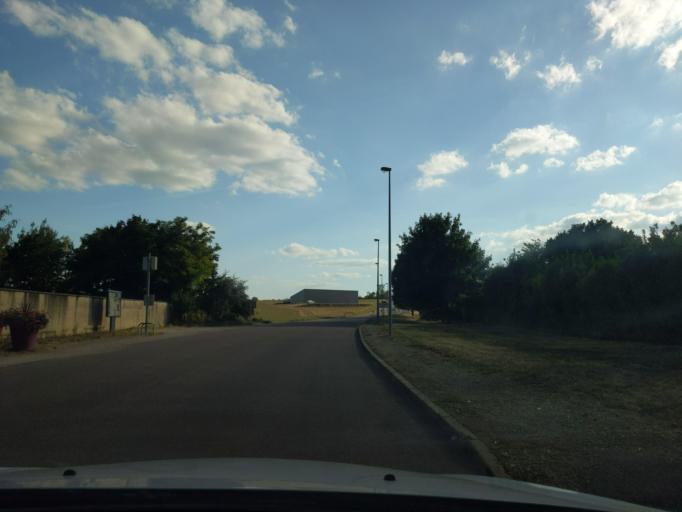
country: FR
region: Bourgogne
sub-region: Departement de la Cote-d'Or
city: Ruffey-les-Echirey
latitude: 47.4043
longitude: 5.0760
